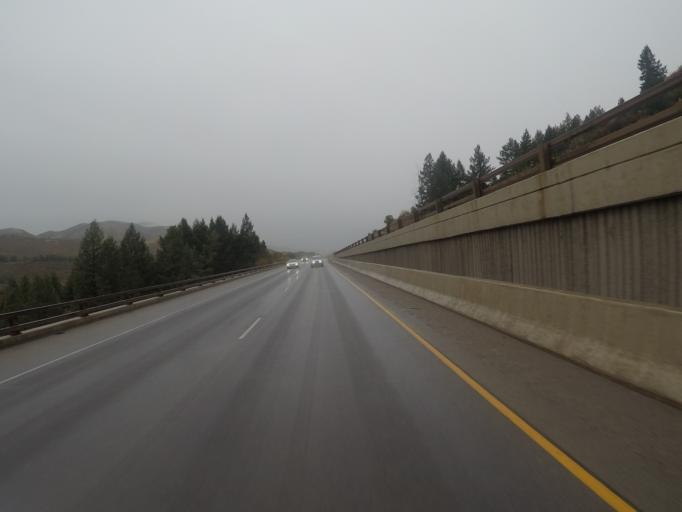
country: US
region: Colorado
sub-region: Pitkin County
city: Snowmass Village
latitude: 39.2426
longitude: -106.8801
